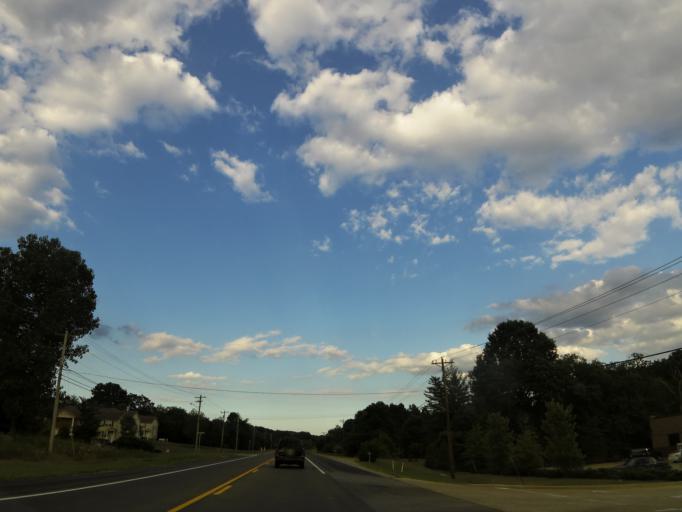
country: US
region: Tennessee
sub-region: Maury County
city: Columbia
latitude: 35.6363
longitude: -86.9674
